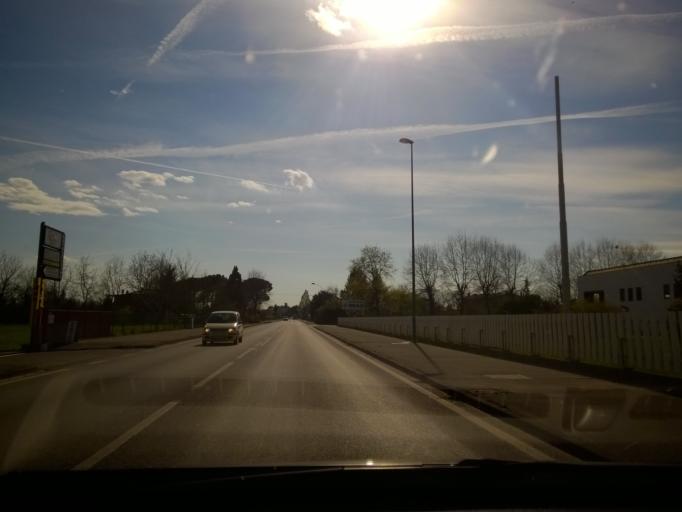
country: IT
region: Veneto
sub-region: Provincia di Treviso
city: Giavera del Montello
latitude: 45.7972
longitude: 12.1766
